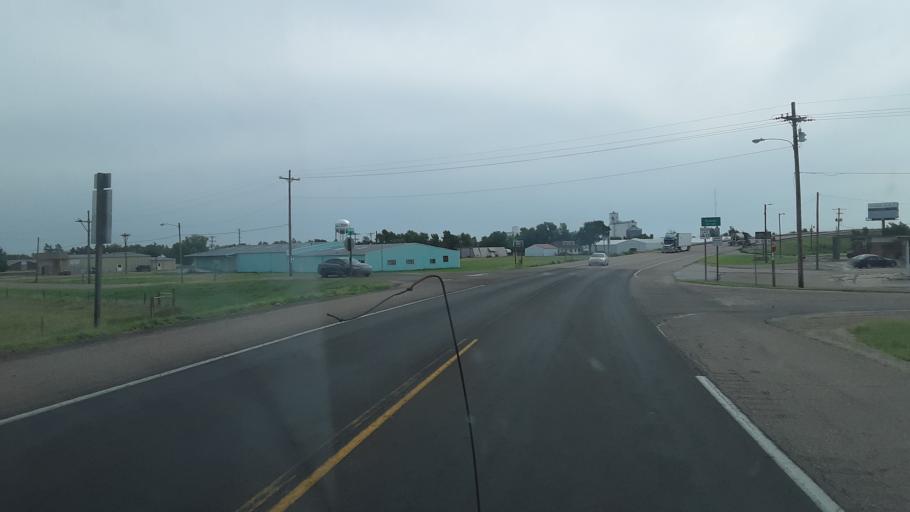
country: US
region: Kansas
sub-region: Edwards County
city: Kinsley
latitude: 37.9179
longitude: -99.4238
